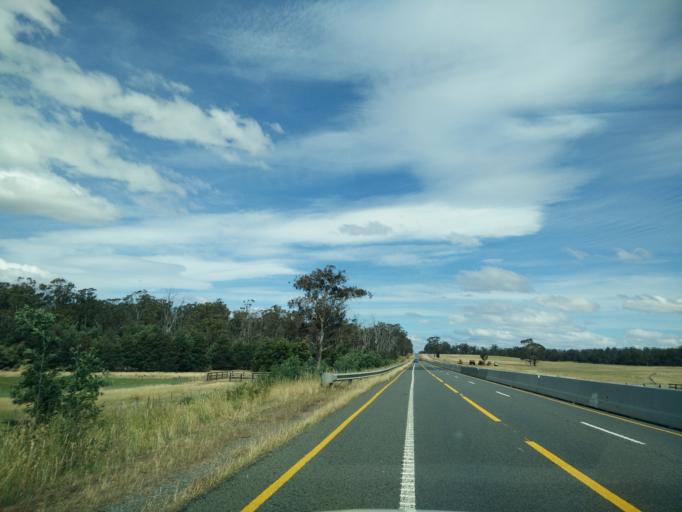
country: AU
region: Tasmania
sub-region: Northern Midlands
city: Evandale
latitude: -41.7413
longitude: 147.3326
